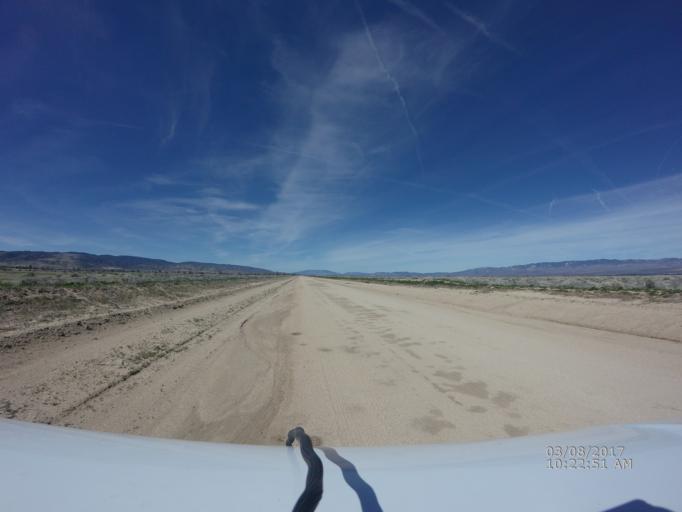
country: US
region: California
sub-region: Los Angeles County
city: Green Valley
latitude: 34.7604
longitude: -118.4348
